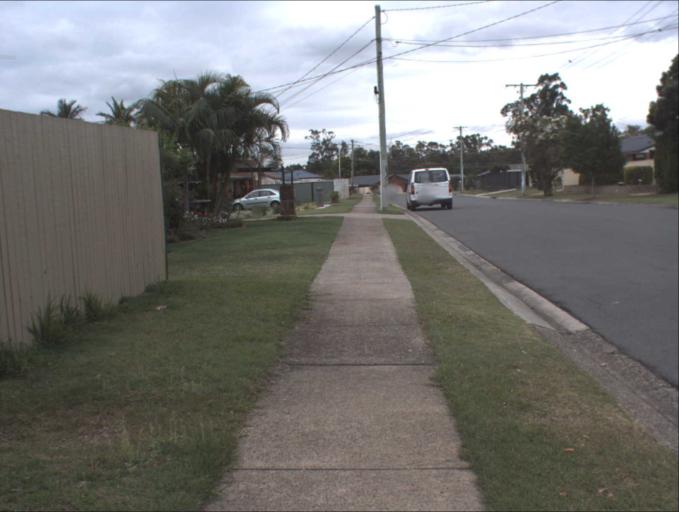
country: AU
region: Queensland
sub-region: Brisbane
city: Sunnybank Hills
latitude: -27.6600
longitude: 153.0222
